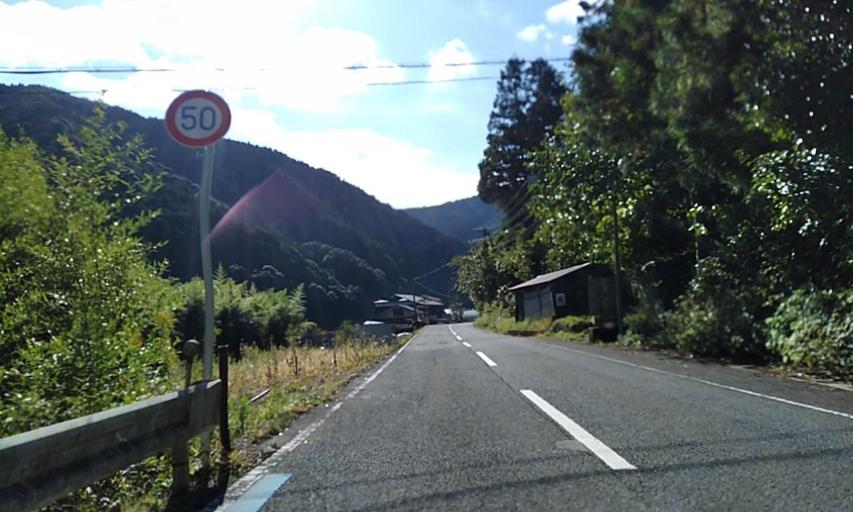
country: JP
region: Wakayama
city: Kainan
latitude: 34.0646
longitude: 135.3582
